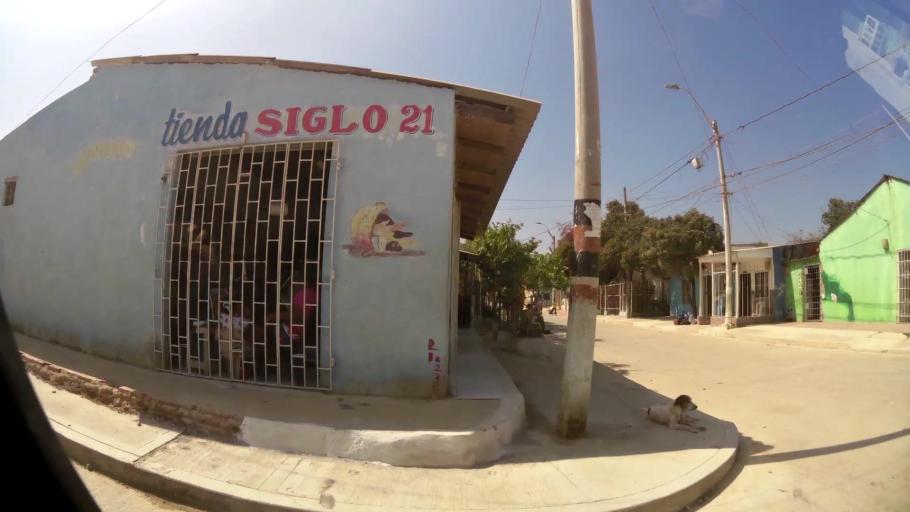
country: CO
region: Atlantico
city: Barranquilla
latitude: 10.9659
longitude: -74.8313
